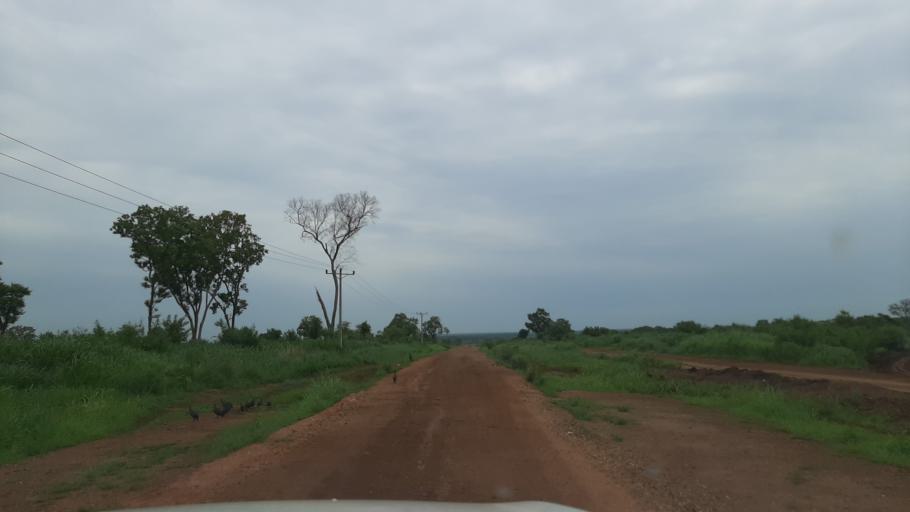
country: ET
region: Gambela
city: Gambela
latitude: 8.1765
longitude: 34.4886
